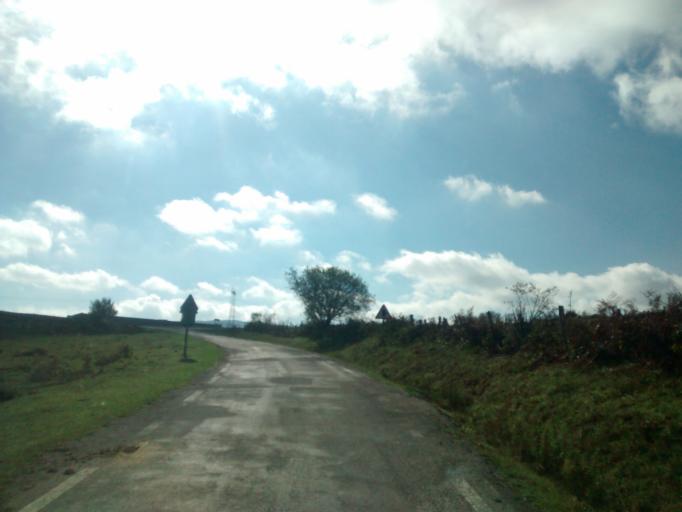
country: ES
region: Castille and Leon
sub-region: Provincia de Burgos
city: Arija
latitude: 42.9252
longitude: -4.0113
